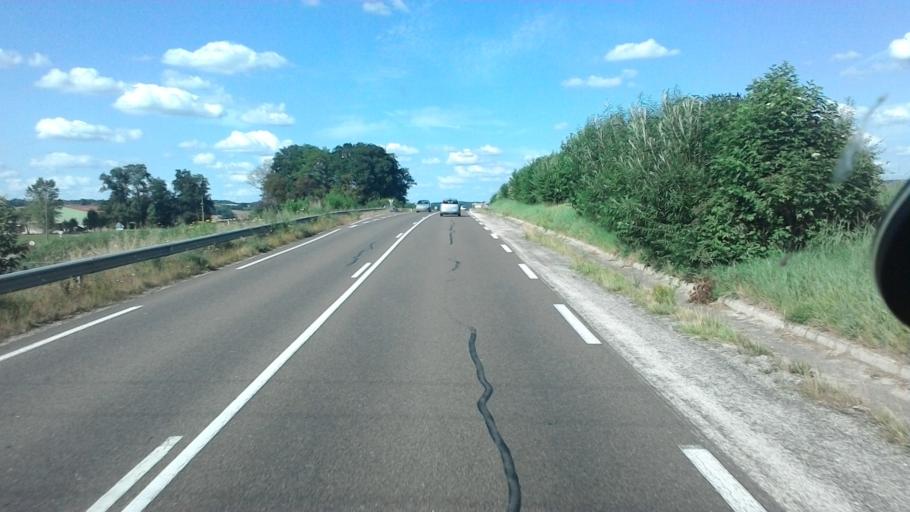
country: FR
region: Franche-Comte
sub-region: Departement de la Haute-Saone
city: Gy
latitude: 47.4142
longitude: 5.8134
